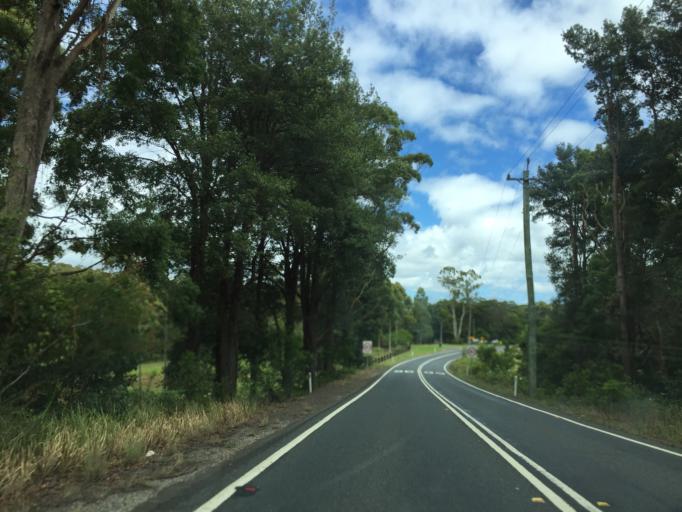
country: AU
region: New South Wales
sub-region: Hawkesbury
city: Richmond
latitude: -33.5196
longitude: 150.6180
